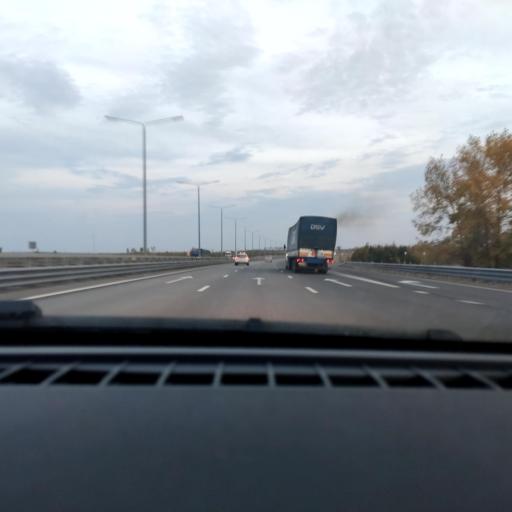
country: RU
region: Voronezj
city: Somovo
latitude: 51.7791
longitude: 39.2965
